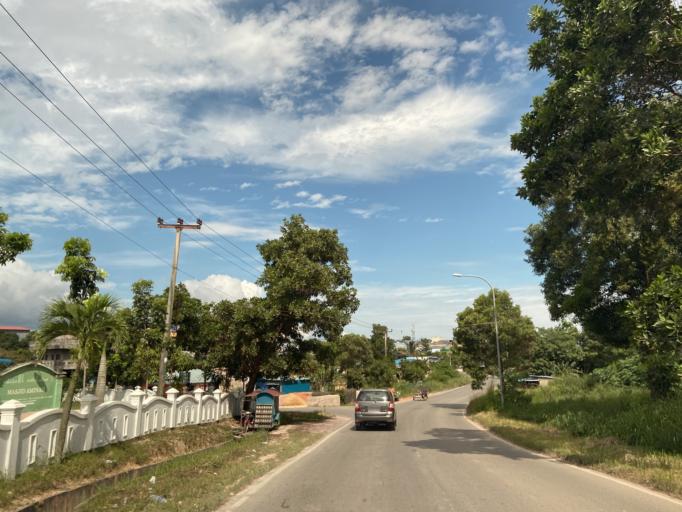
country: SG
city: Singapore
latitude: 1.0298
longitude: 103.9433
